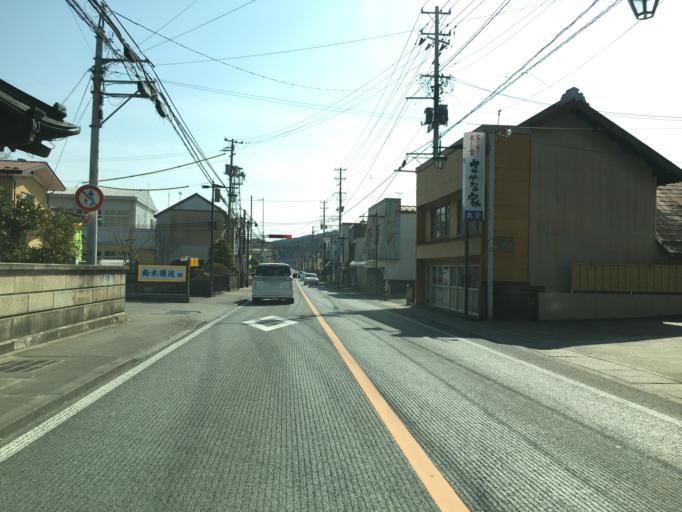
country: JP
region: Ibaraki
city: Daigo
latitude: 36.8720
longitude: 140.4244
